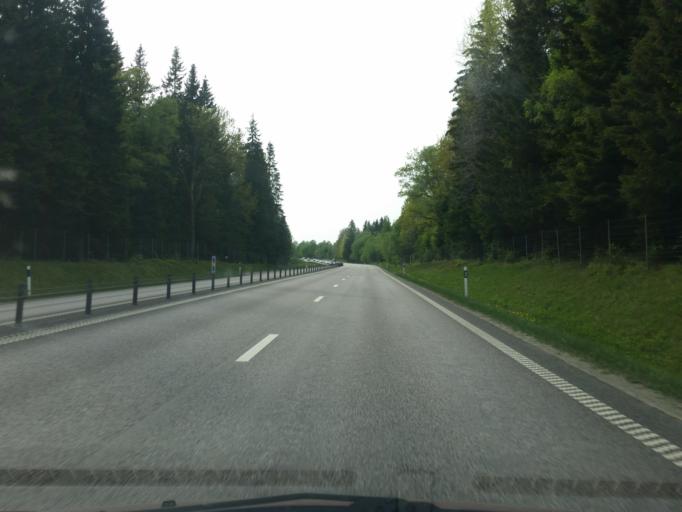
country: SE
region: Vaestra Goetaland
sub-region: Ulricehamns Kommun
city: Ulricehamn
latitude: 57.7990
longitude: 13.5278
